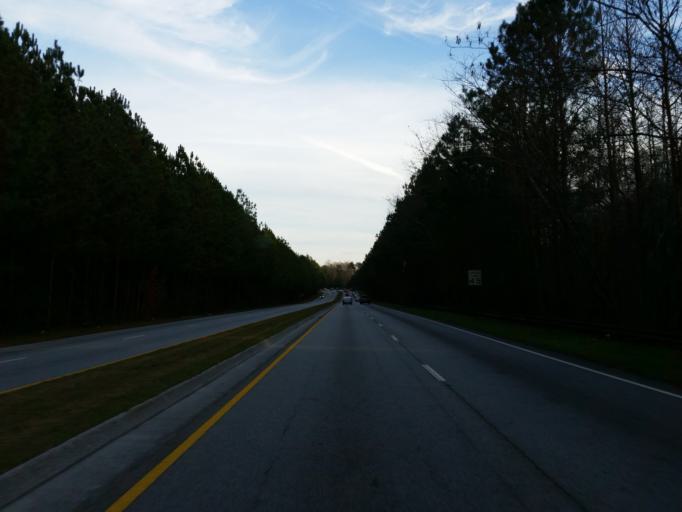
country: US
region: Georgia
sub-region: Cobb County
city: Mableton
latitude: 33.8483
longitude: -84.5517
